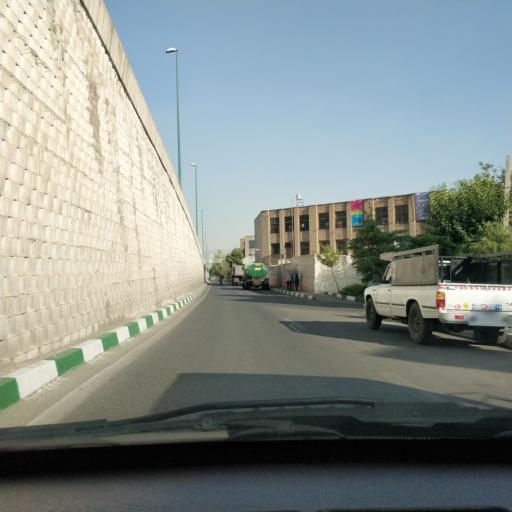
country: IR
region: Tehran
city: Tehran
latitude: 35.7219
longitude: 51.4742
